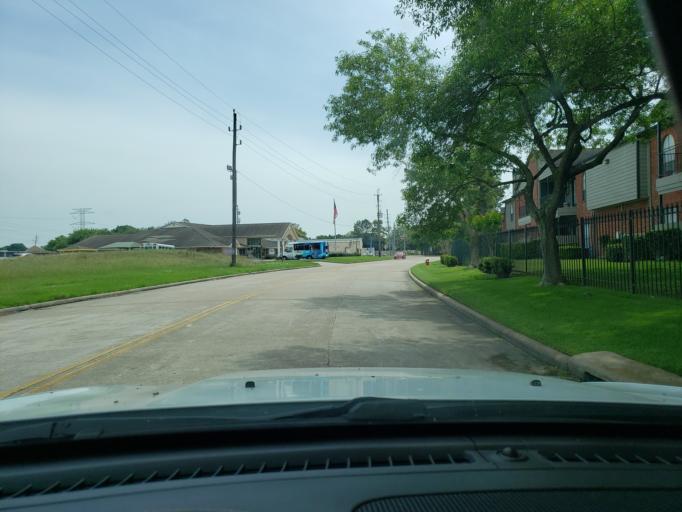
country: US
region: Texas
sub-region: Harris County
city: Jersey Village
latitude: 29.9115
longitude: -95.5800
